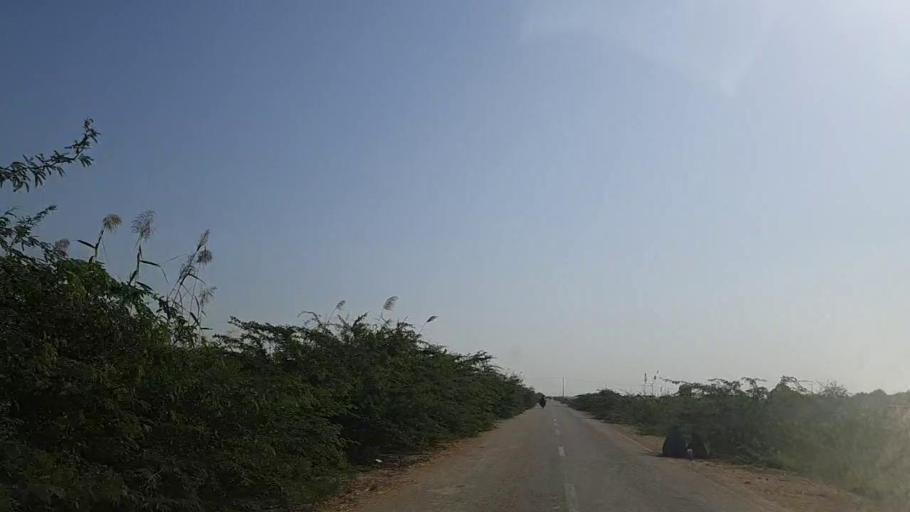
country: PK
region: Sindh
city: Jati
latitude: 24.5127
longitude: 68.2746
